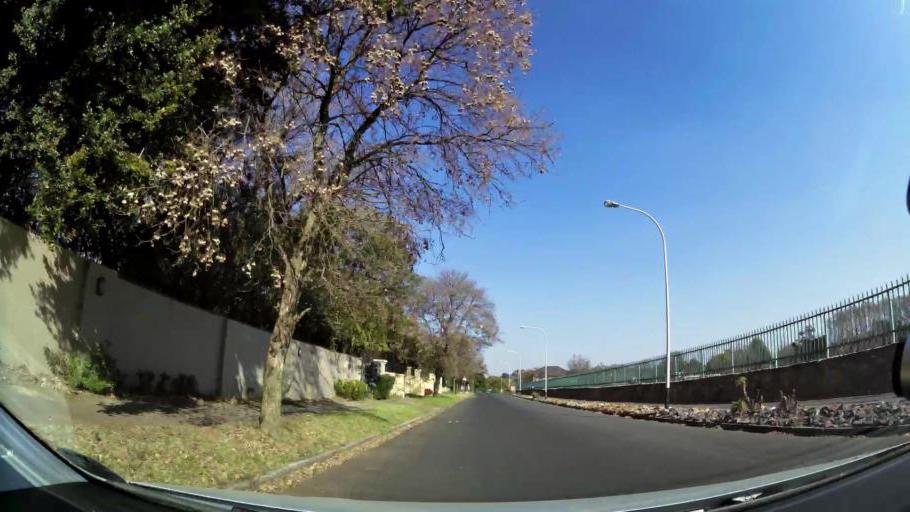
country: ZA
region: Gauteng
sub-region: City of Johannesburg Metropolitan Municipality
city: Johannesburg
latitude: -26.1728
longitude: 28.0789
